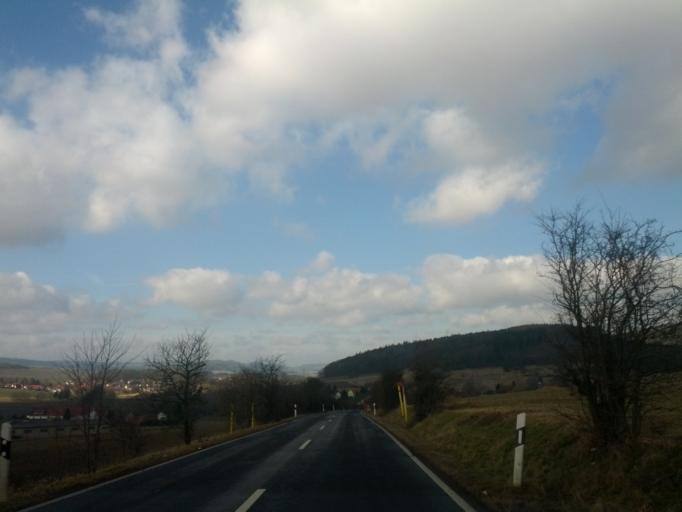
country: DE
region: Thuringia
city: Krauthausen
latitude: 51.0131
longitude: 10.2936
